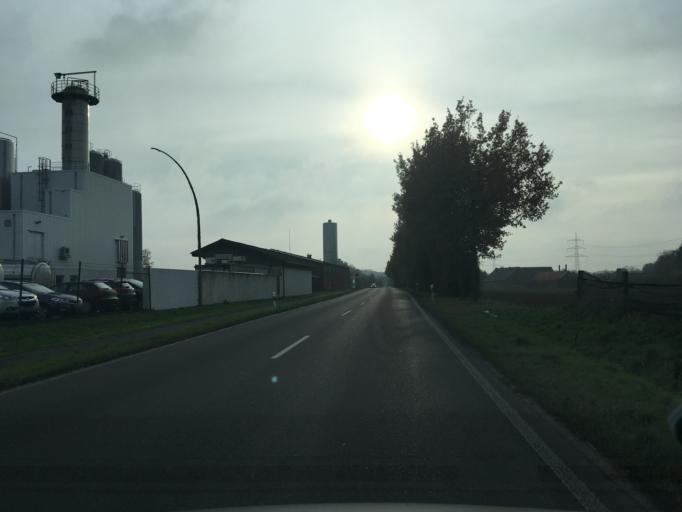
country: DE
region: North Rhine-Westphalia
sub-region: Regierungsbezirk Munster
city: Velen
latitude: 51.8988
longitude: 6.9752
